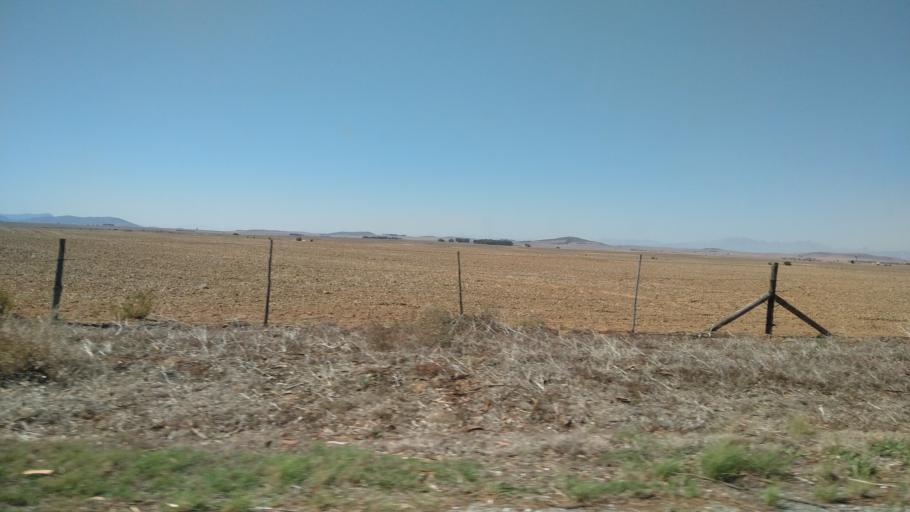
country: ZA
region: Western Cape
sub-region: West Coast District Municipality
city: Moorreesburg
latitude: -33.2328
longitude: 18.5606
